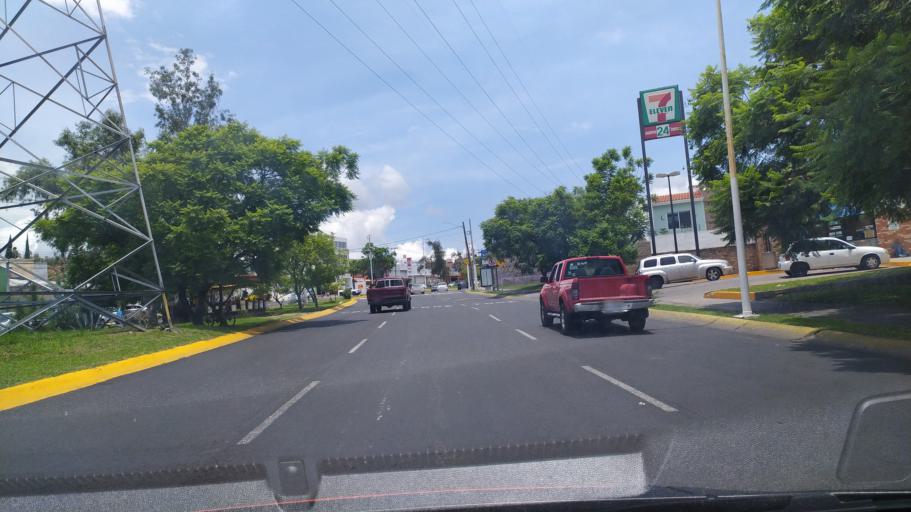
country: MX
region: Jalisco
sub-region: Zapopan
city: Zapopan
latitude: 20.7567
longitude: -103.3871
